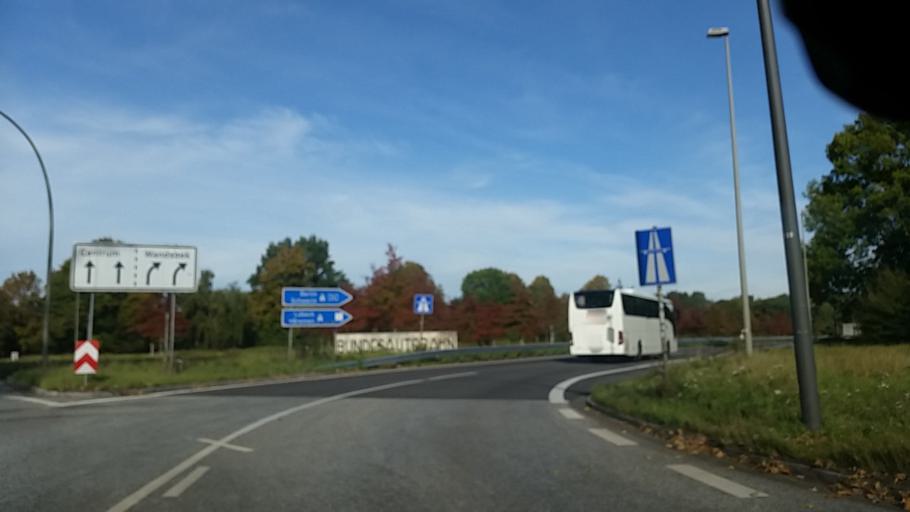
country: DE
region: Hamburg
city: Marienthal
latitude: 53.5592
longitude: 10.0712
